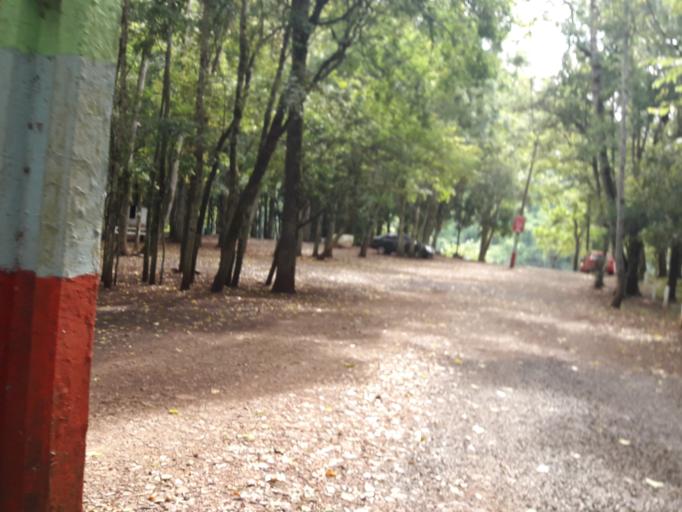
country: BR
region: Rio Grande do Sul
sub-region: Frederico Westphalen
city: Frederico Westphalen
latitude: -27.0886
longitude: -53.3771
